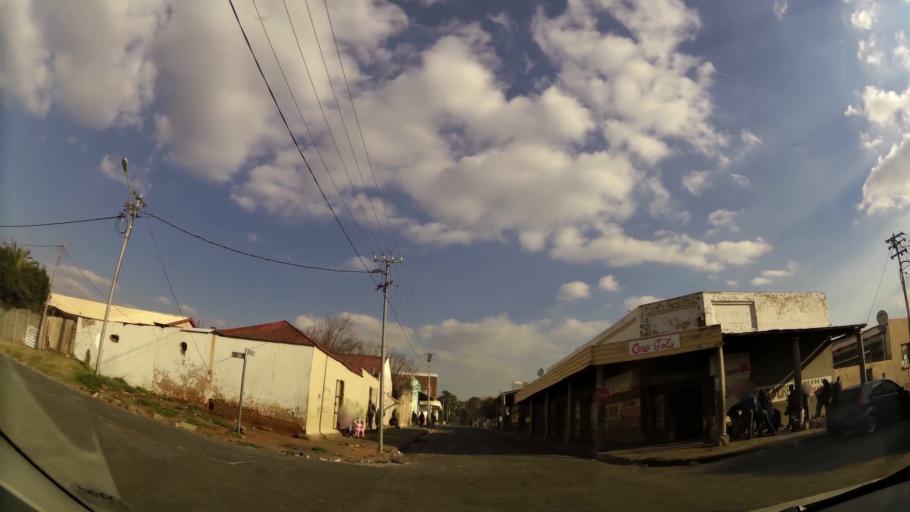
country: ZA
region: Gauteng
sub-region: West Rand District Municipality
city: Krugersdorp
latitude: -26.0971
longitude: 27.7584
